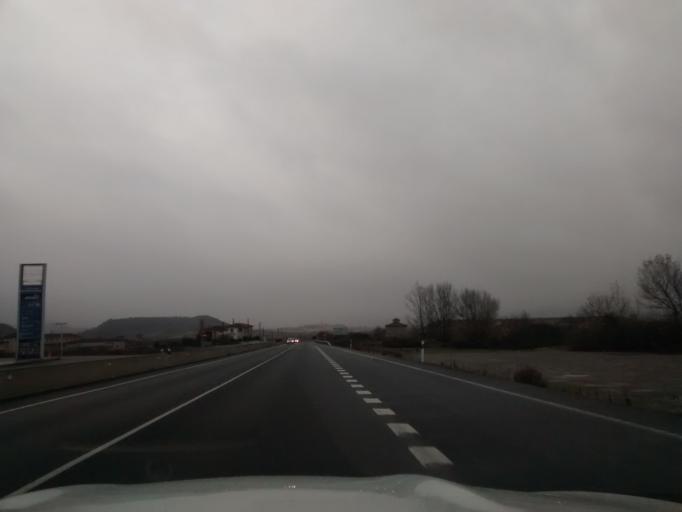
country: ES
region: La Rioja
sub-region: Provincia de La Rioja
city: San Asensio
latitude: 42.5140
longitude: -2.7412
